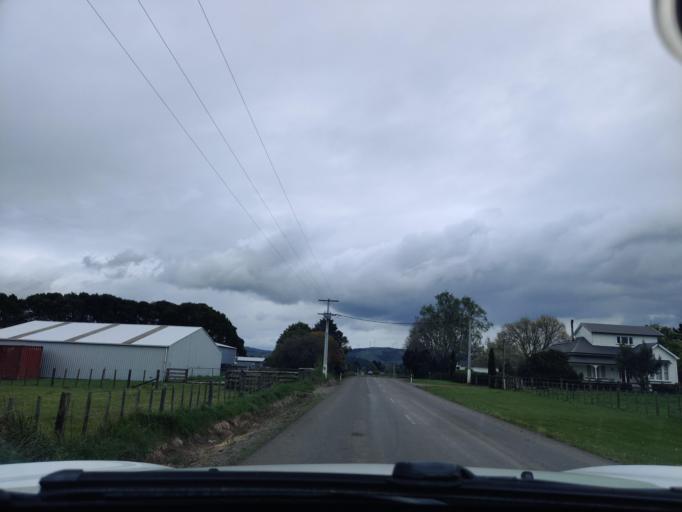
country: NZ
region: Manawatu-Wanganui
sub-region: Palmerston North City
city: Palmerston North
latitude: -40.3235
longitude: 175.8850
